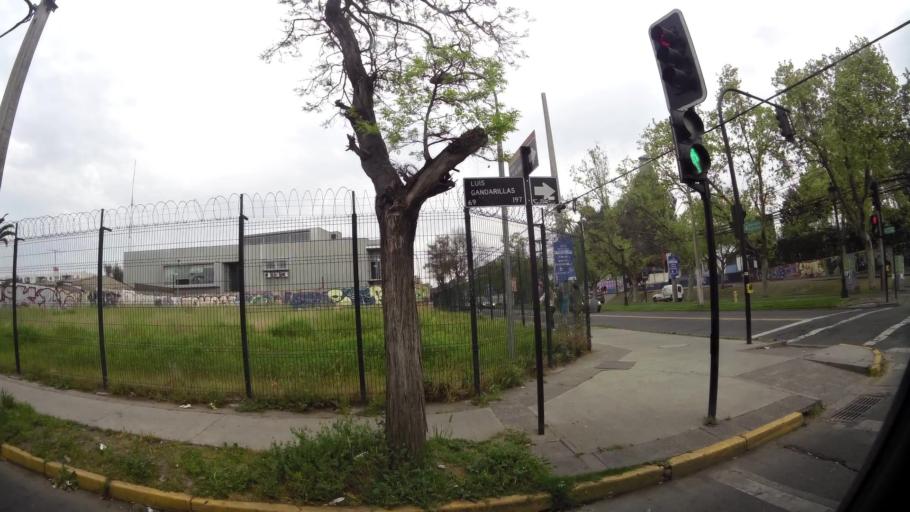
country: CL
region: Santiago Metropolitan
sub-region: Provincia de Santiago
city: Lo Prado
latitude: -33.5037
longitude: -70.7573
